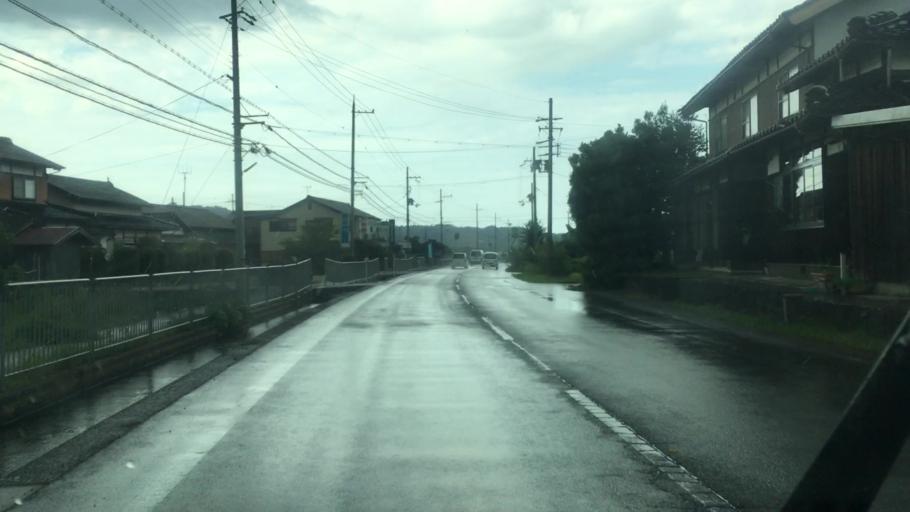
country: JP
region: Hyogo
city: Toyooka
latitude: 35.4909
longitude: 134.8158
